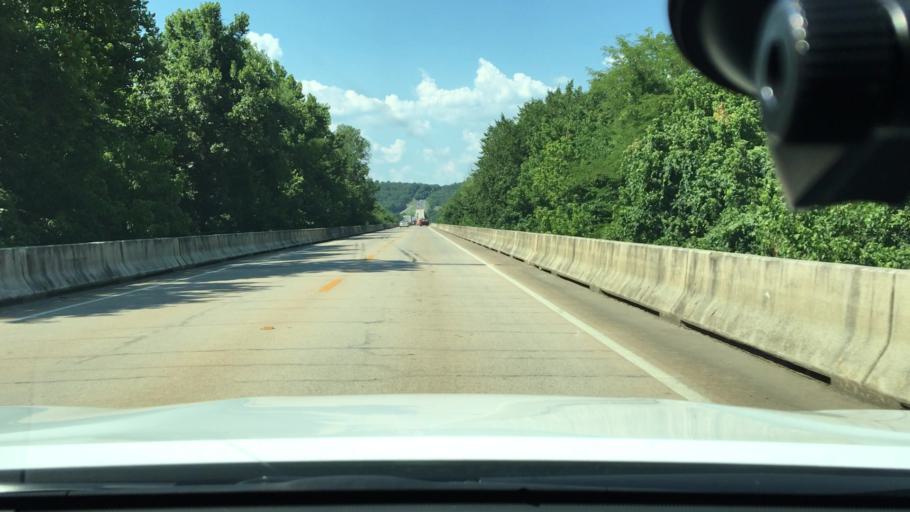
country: US
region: Arkansas
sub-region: Johnson County
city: Clarksville
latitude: 35.4009
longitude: -93.5311
